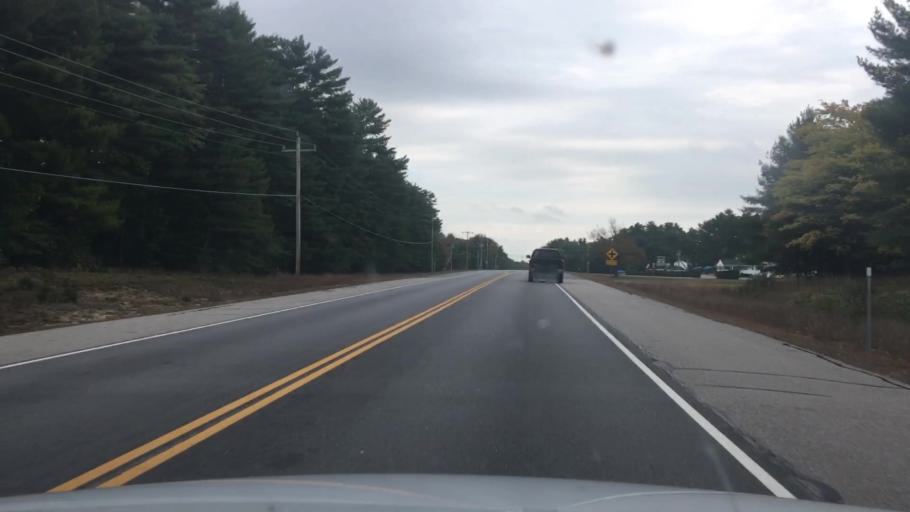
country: US
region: New Hampshire
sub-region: Strafford County
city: New Durham
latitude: 43.4322
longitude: -71.1675
